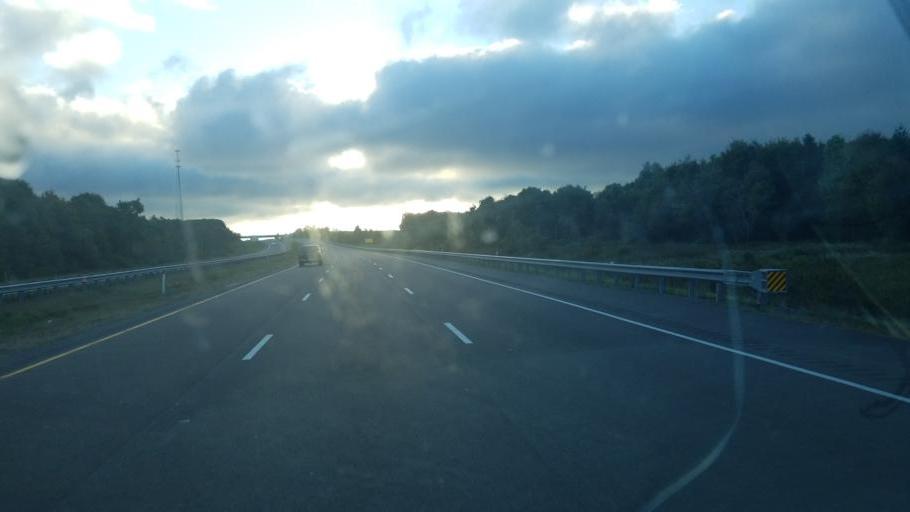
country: US
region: Maryland
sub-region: Allegany County
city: Frostburg
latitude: 39.6833
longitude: -79.0113
